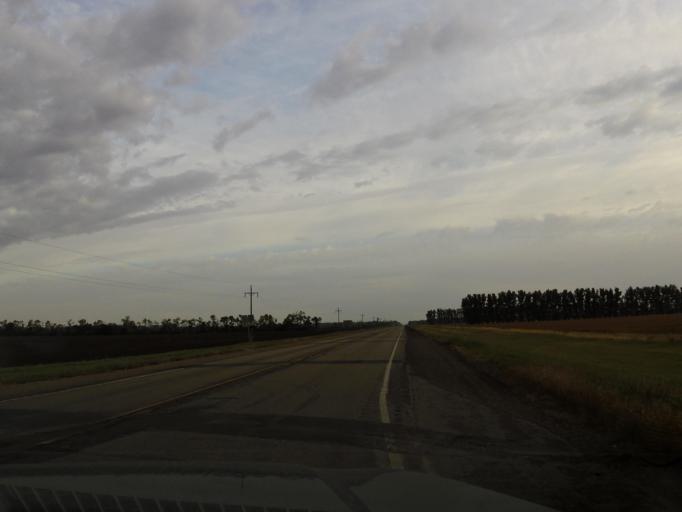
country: US
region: North Dakota
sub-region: Pembina County
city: Cavalier
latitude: 48.6013
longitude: -97.6230
